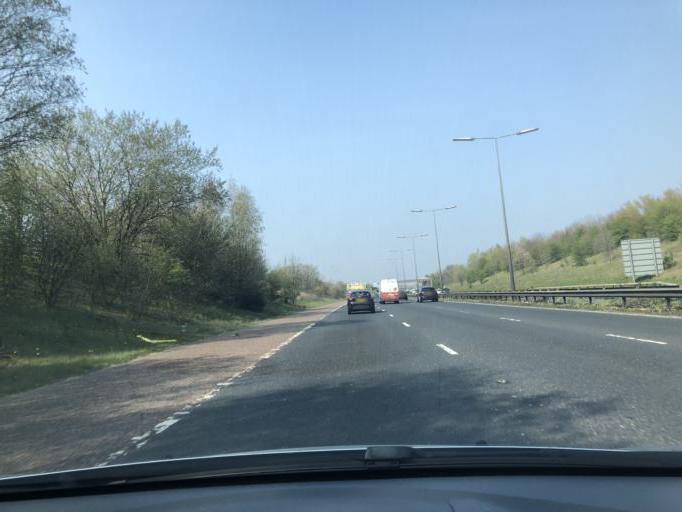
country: GB
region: England
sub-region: Borough of Tameside
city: Denton
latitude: 53.4442
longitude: -2.1334
